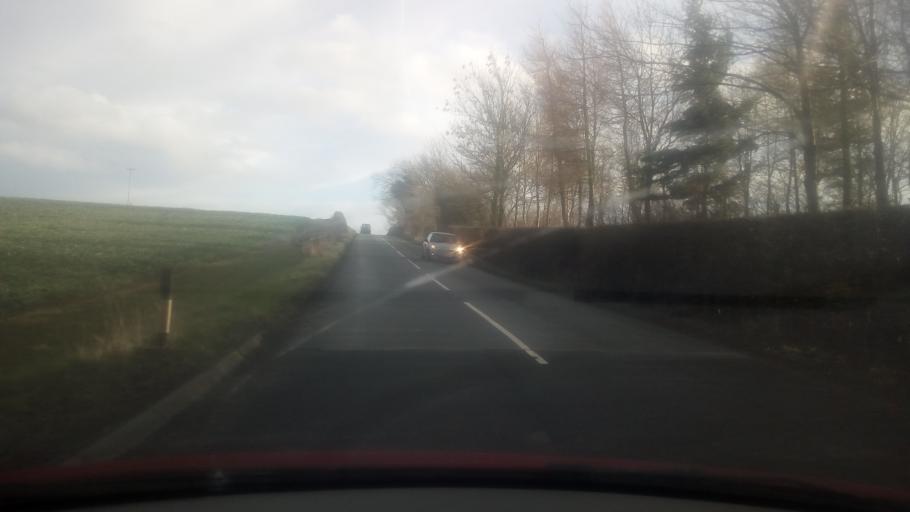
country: GB
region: Scotland
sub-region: The Scottish Borders
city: Coldstream
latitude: 55.7133
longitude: -2.2824
